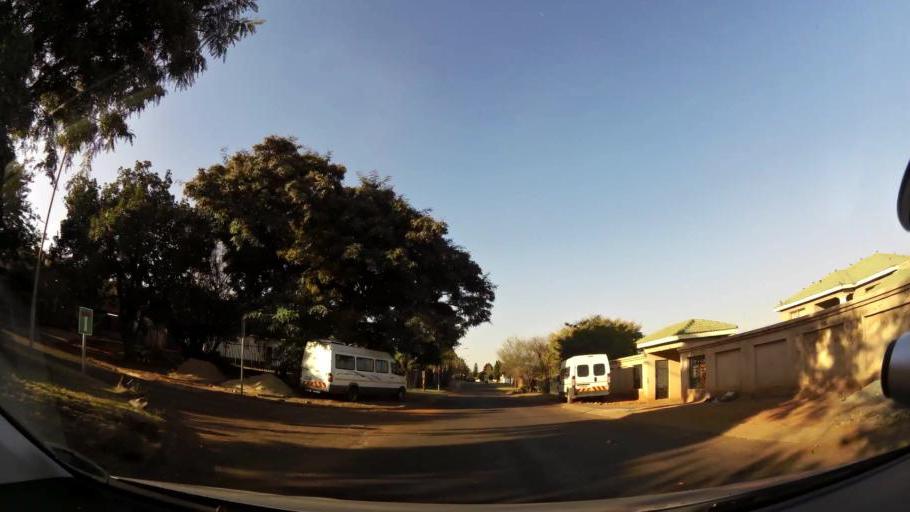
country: ZA
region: Gauteng
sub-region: City of Tshwane Metropolitan Municipality
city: Pretoria
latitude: -25.7328
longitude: 28.1276
